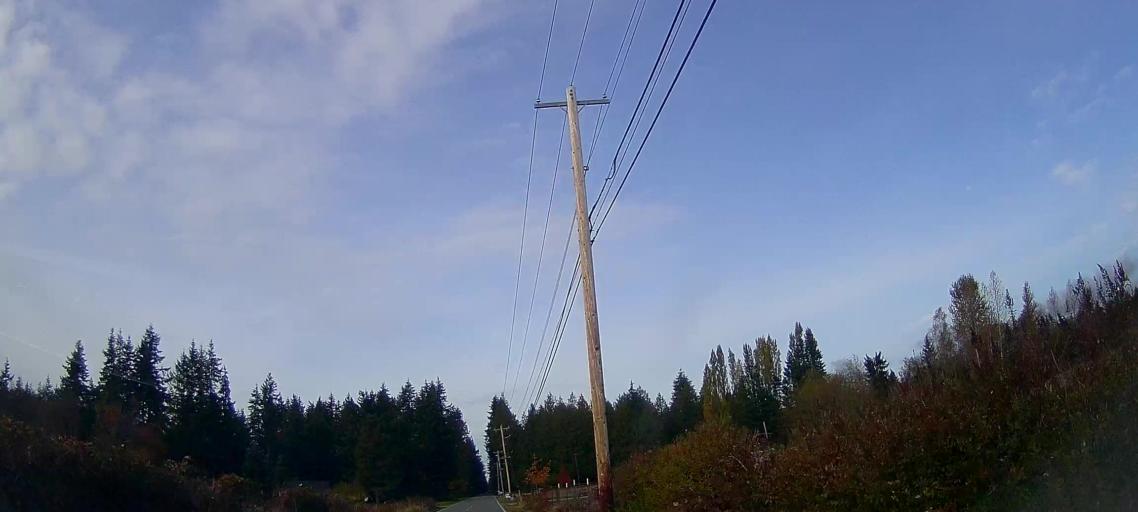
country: US
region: Washington
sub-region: Snohomish County
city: Stanwood
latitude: 48.2751
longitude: -122.3364
